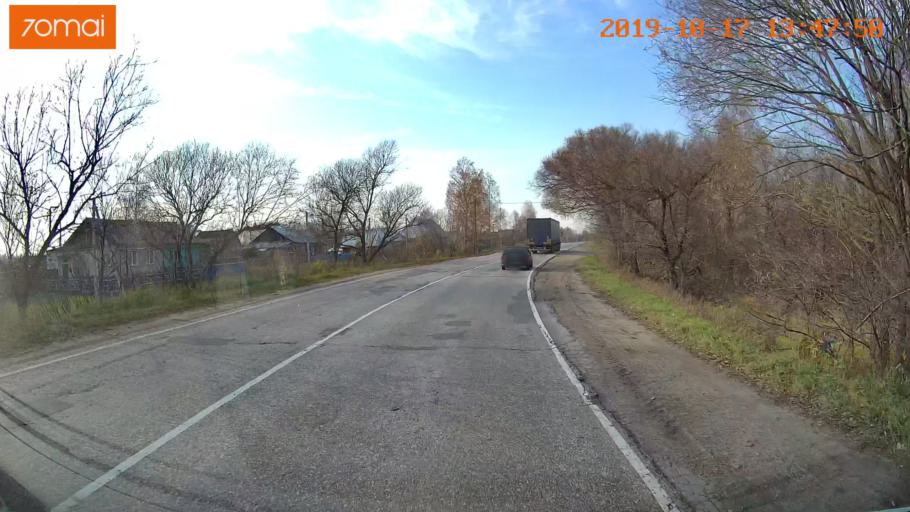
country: RU
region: Rjazan
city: Tuma
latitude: 55.1457
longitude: 40.4656
